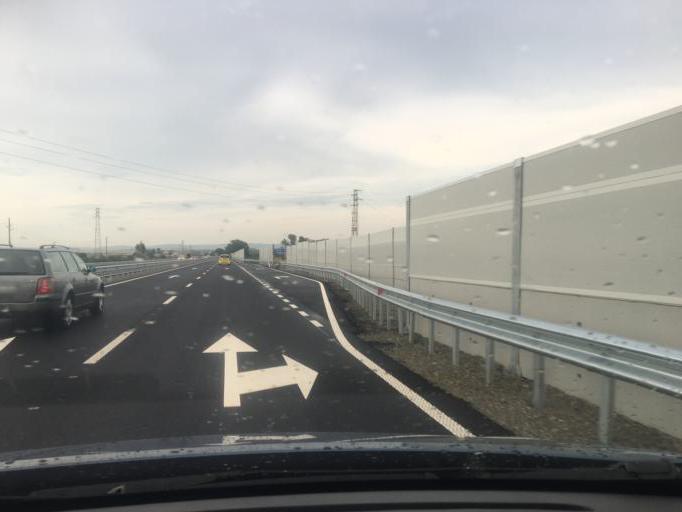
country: BG
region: Burgas
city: Aheloy
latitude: 42.6332
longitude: 27.6356
